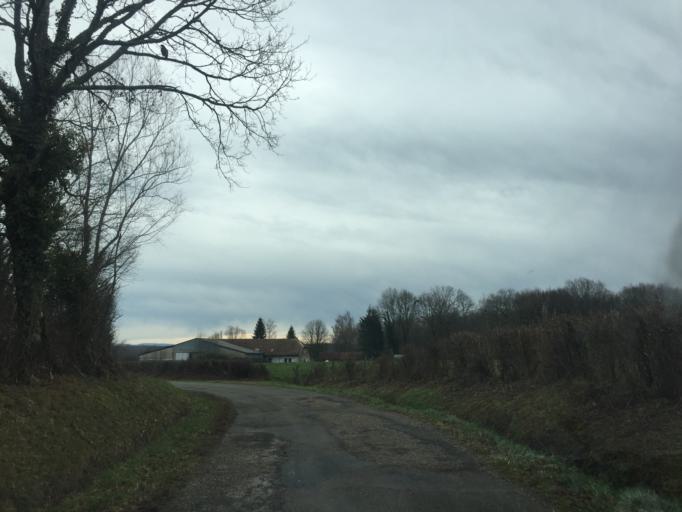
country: FR
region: Franche-Comte
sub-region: Departement du Jura
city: Mont-sous-Vaudrey
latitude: 46.8653
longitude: 5.5282
